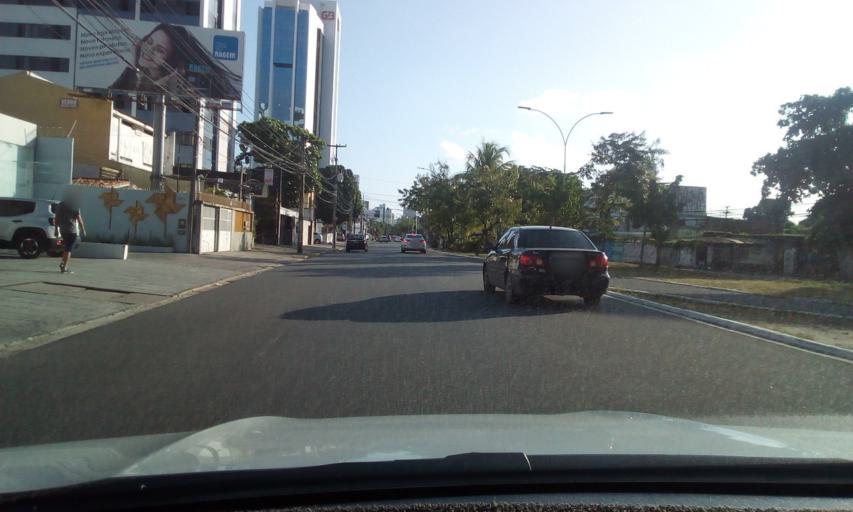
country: BR
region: Pernambuco
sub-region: Recife
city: Recife
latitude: -8.0977
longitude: -34.8860
